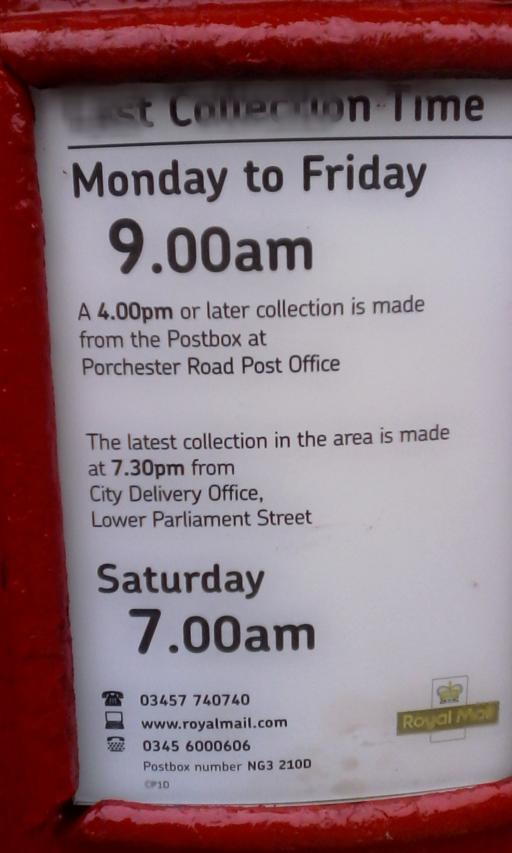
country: GB
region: England
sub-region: Nottinghamshire
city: Arnold
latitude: 52.9762
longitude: -1.1180
